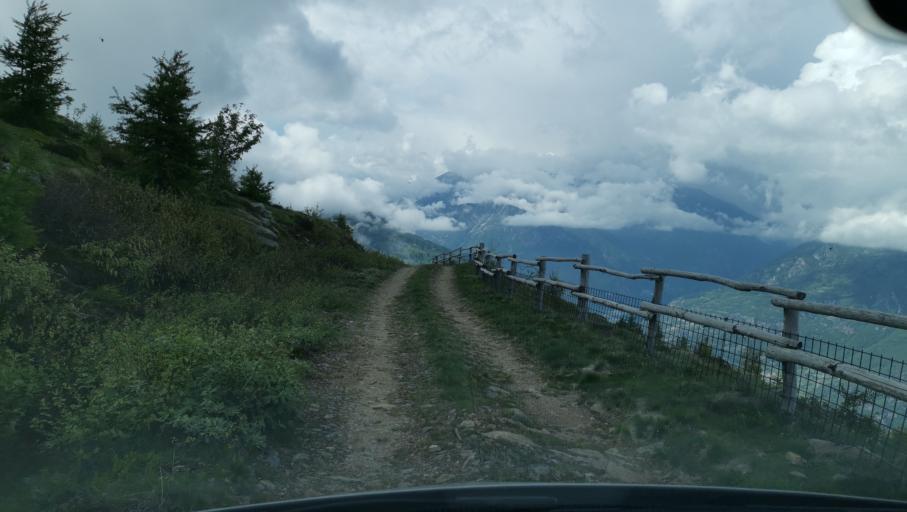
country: IT
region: Piedmont
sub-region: Provincia di Torino
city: Quincinetto
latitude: 45.5323
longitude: 7.7905
